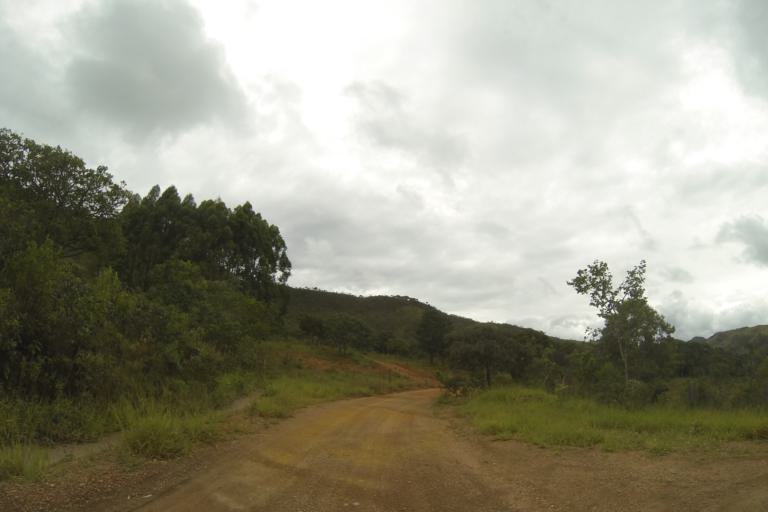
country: BR
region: Minas Gerais
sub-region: Ibia
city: Ibia
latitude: -19.7547
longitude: -46.5013
